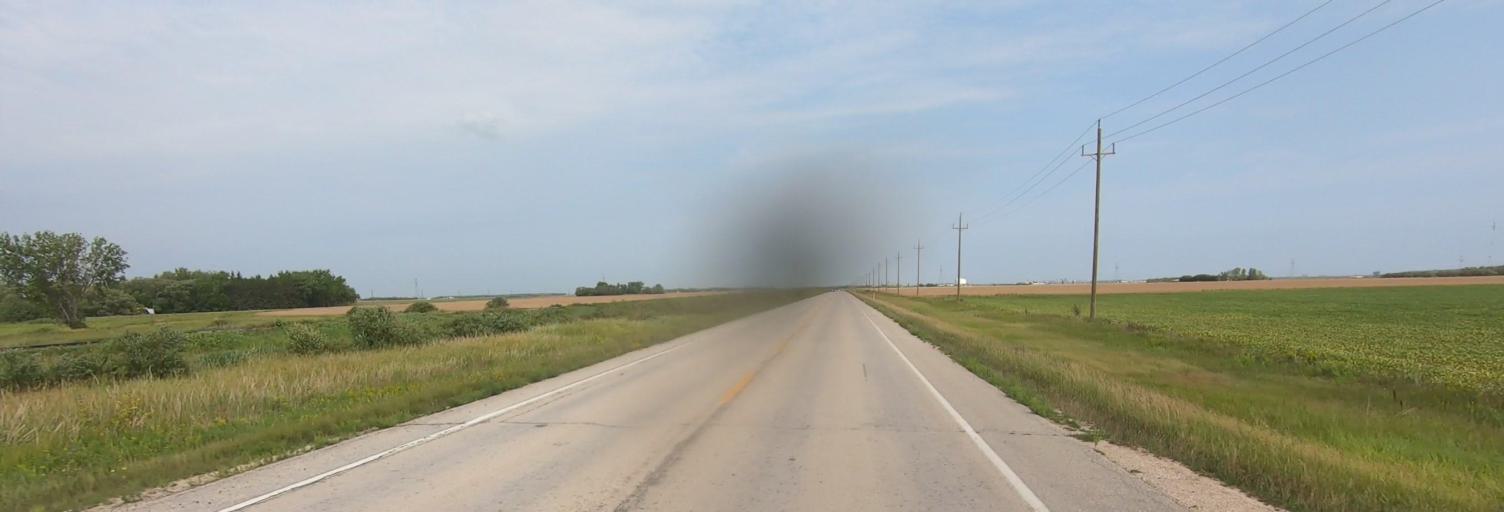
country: CA
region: Manitoba
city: Winnipeg
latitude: 49.7298
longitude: -97.2519
